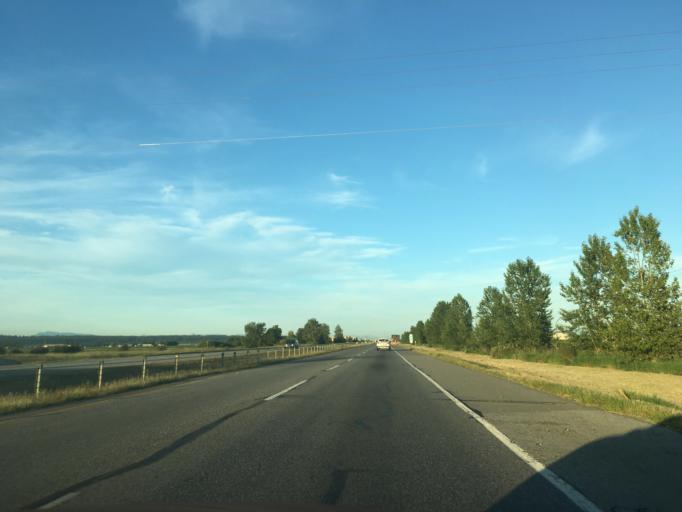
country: CA
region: British Columbia
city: Delta
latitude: 49.0904
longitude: -122.9798
